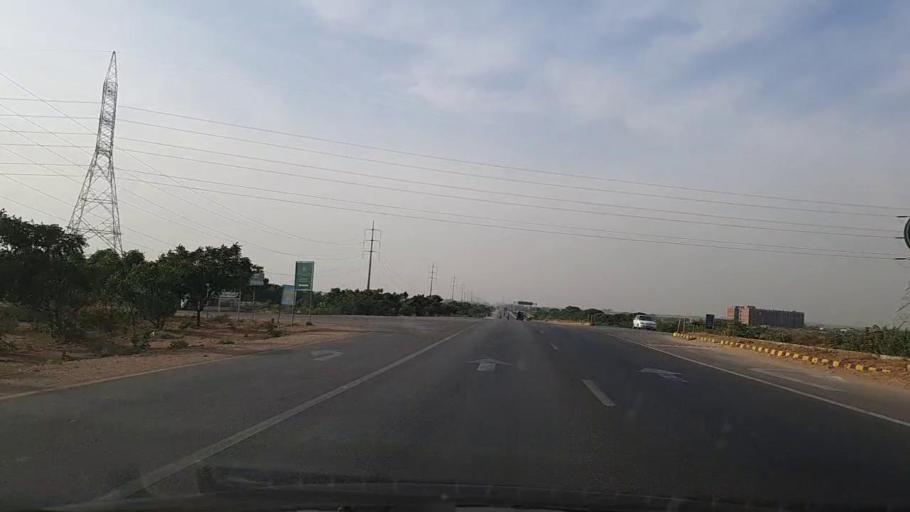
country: PK
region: Sindh
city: Gharo
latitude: 24.7680
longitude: 67.5499
